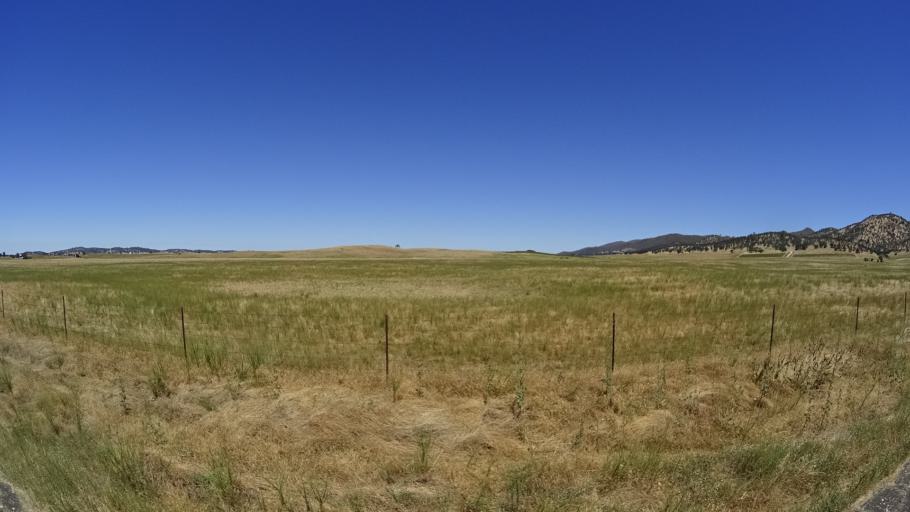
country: US
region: California
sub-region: Calaveras County
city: Copperopolis
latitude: 38.0380
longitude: -120.7033
